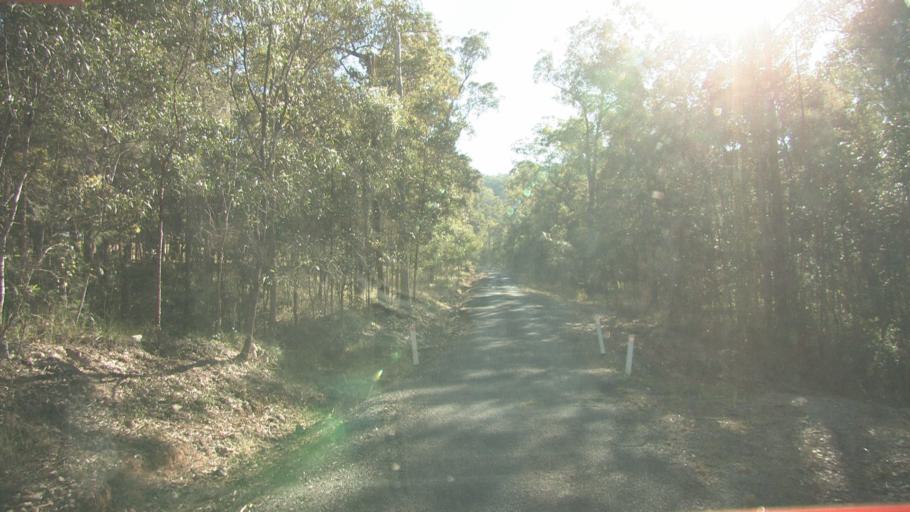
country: AU
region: Queensland
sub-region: Logan
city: Windaroo
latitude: -27.7897
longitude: 153.1714
